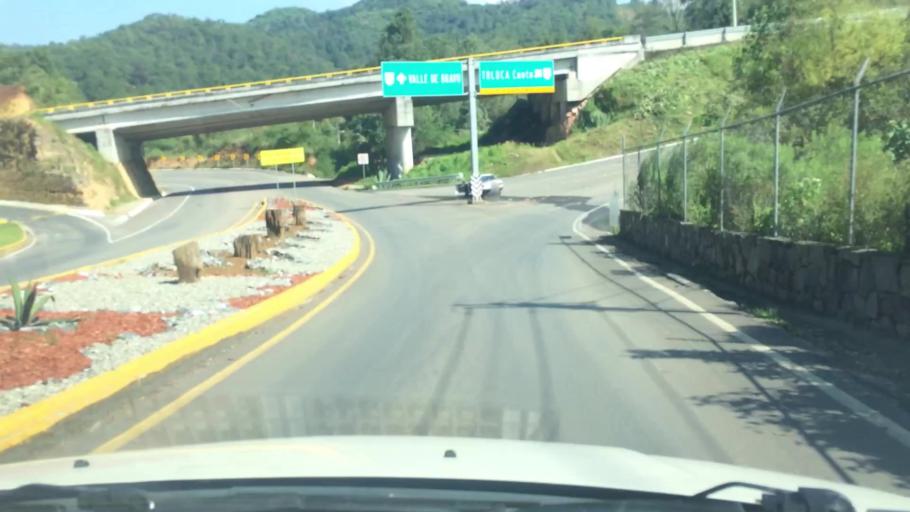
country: MX
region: Mexico
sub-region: Valle de Bravo
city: Colonia Rincon Villa del Valle
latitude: 19.2026
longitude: -100.1009
